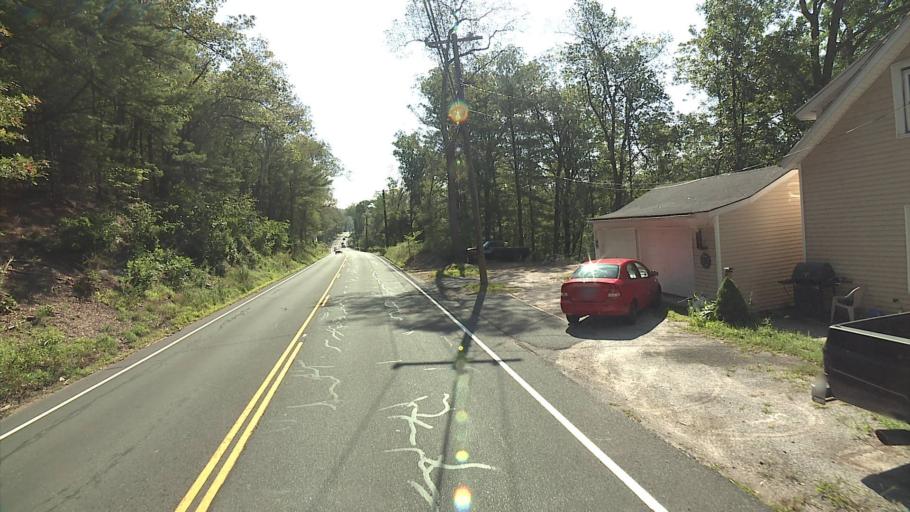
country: US
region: Connecticut
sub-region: Tolland County
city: Somers
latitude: 41.9831
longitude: -72.4201
